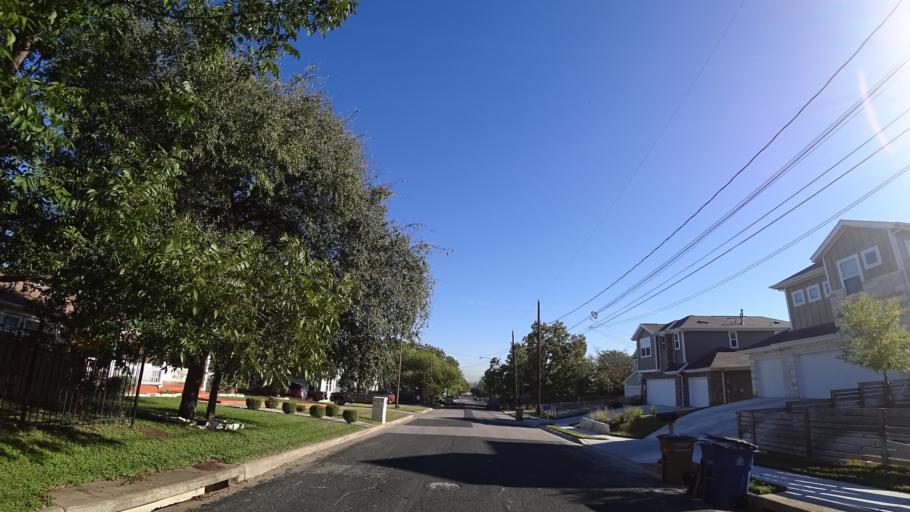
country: US
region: Texas
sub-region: Travis County
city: Austin
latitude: 30.2196
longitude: -97.7002
